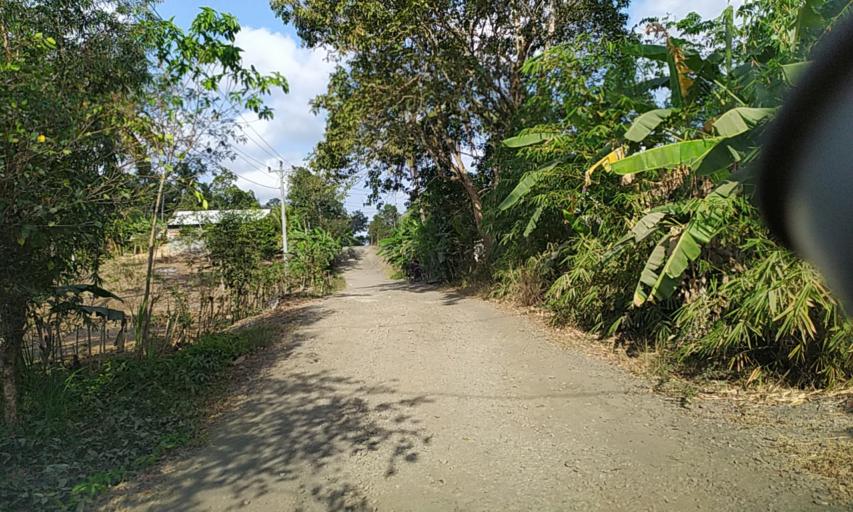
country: ID
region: Central Java
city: Jeruklegi
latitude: -7.6471
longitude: 108.9716
